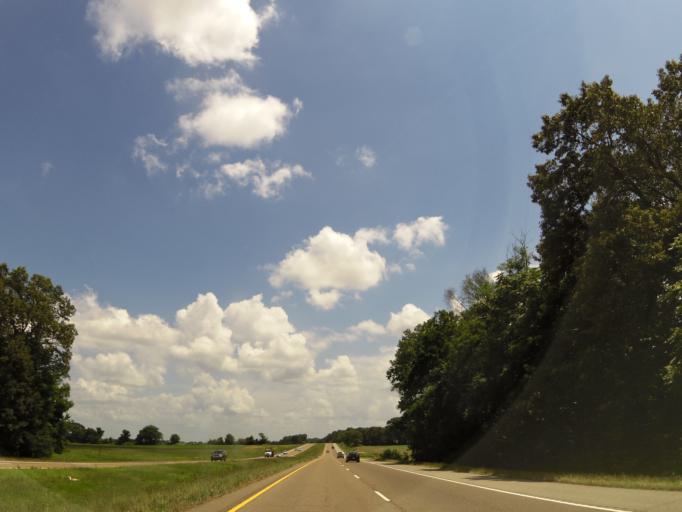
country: US
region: Tennessee
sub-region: Crockett County
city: Alamo
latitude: 35.7659
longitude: -89.1185
